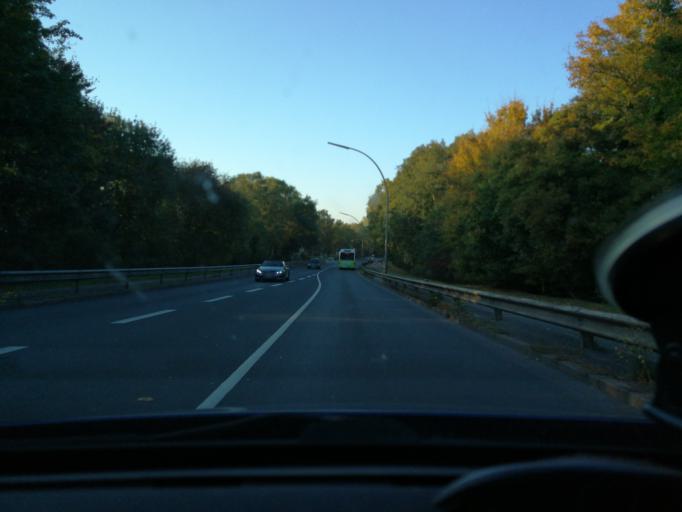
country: DE
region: Hamburg
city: Altona
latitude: 53.4744
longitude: 9.9004
